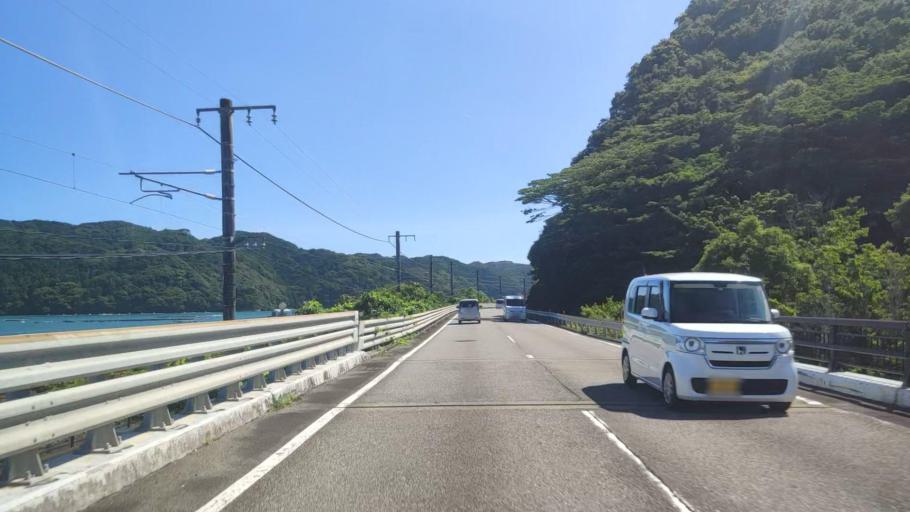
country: JP
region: Wakayama
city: Shingu
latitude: 33.5673
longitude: 135.9093
